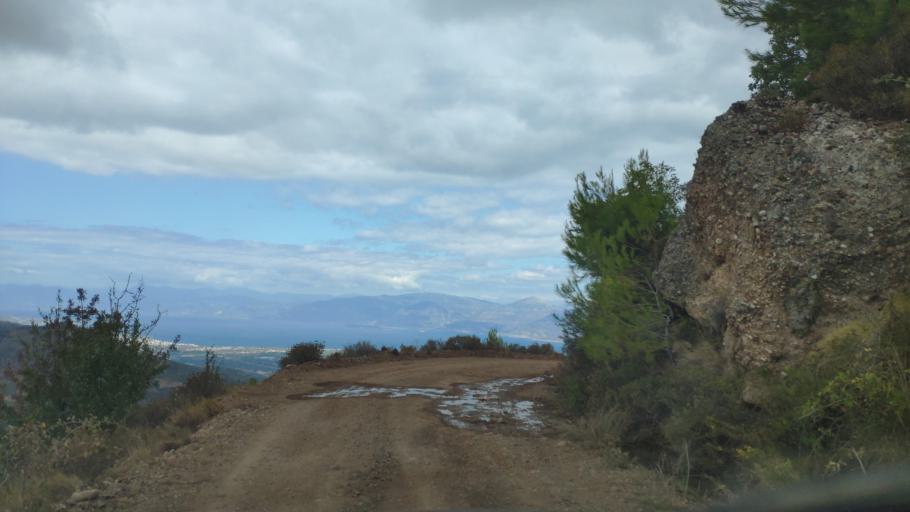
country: GR
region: West Greece
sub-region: Nomos Achaias
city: Temeni
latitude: 38.1692
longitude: 22.1533
